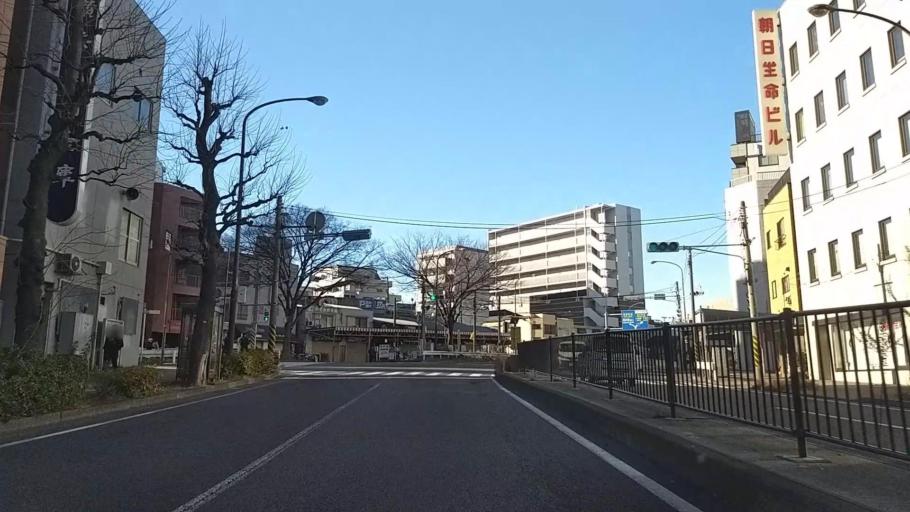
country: JP
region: Kanagawa
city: Yokohama
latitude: 35.4754
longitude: 139.6266
